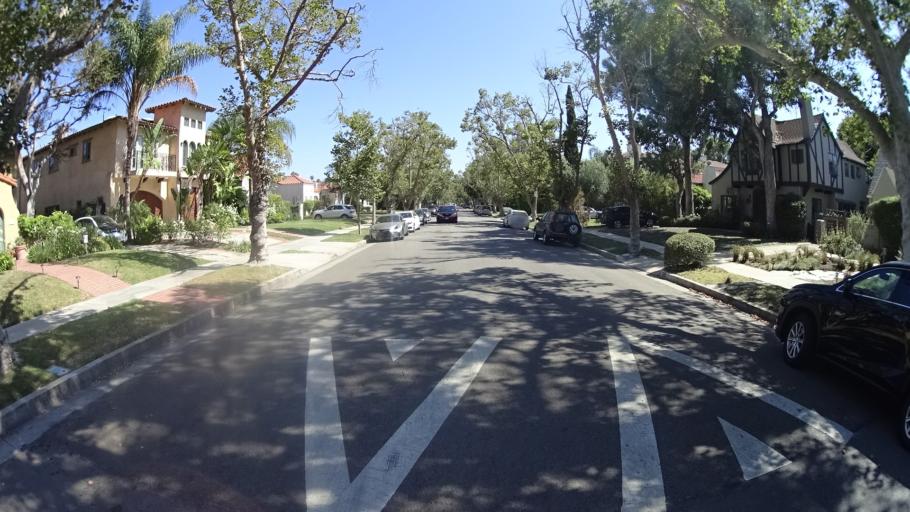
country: US
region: California
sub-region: Los Angeles County
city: Hollywood
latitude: 34.0772
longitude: -118.3397
